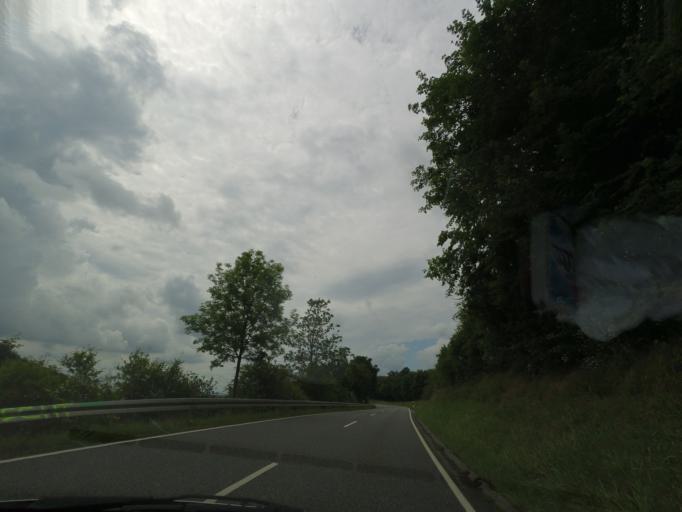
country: DE
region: Hesse
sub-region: Regierungsbezirk Giessen
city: Heuchelheim
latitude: 50.6148
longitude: 8.6275
